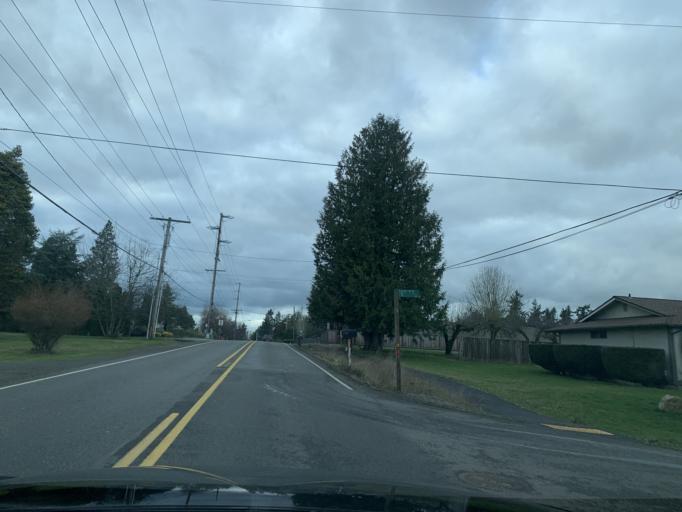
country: US
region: Washington
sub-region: Pierce County
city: Milton
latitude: 47.2356
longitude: -122.3024
